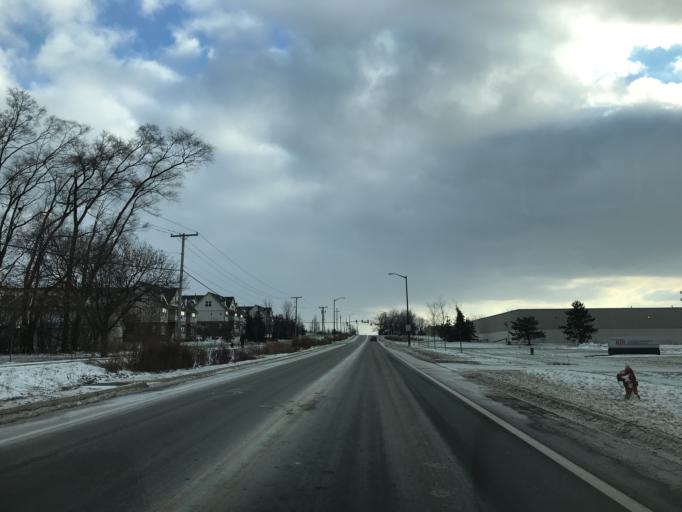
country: US
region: Michigan
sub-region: Washtenaw County
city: Ann Arbor
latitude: 42.2325
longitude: -83.7196
